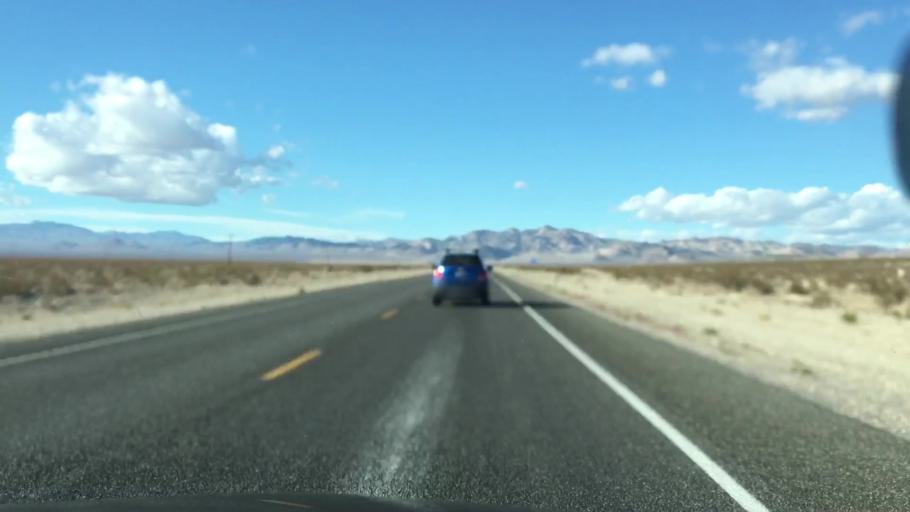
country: US
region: Nevada
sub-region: Nye County
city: Beatty
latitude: 36.8152
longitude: -116.7324
